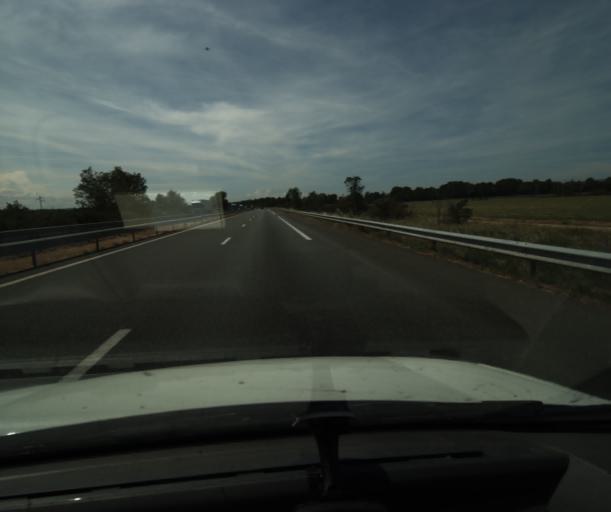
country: FR
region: Languedoc-Roussillon
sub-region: Departement de l'Aude
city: Montreal
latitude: 43.2271
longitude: 2.1507
